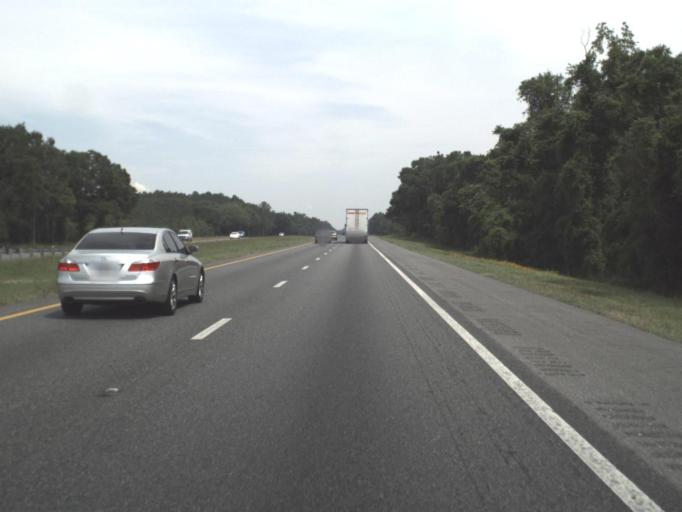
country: US
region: Florida
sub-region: Suwannee County
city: Live Oak
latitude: 30.3118
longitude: -82.9335
